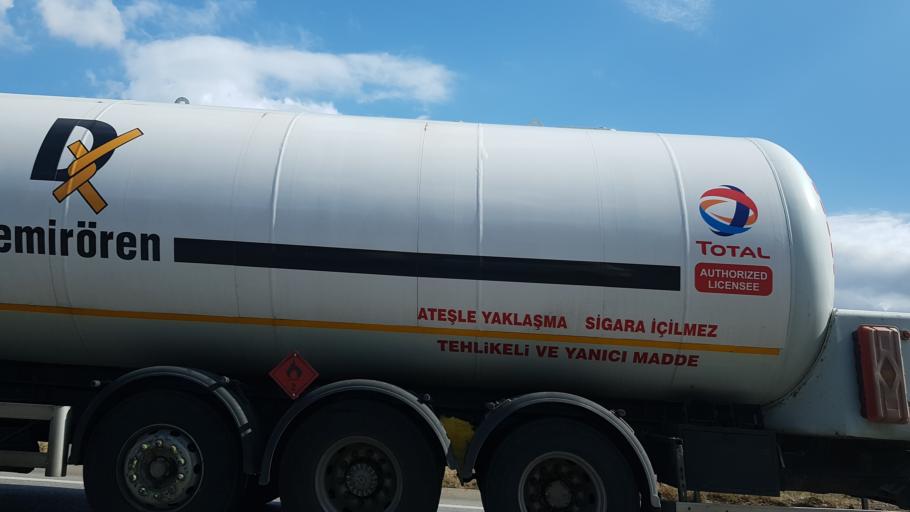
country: TR
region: Bursa
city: Demirtas
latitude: 40.3434
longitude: 29.1105
